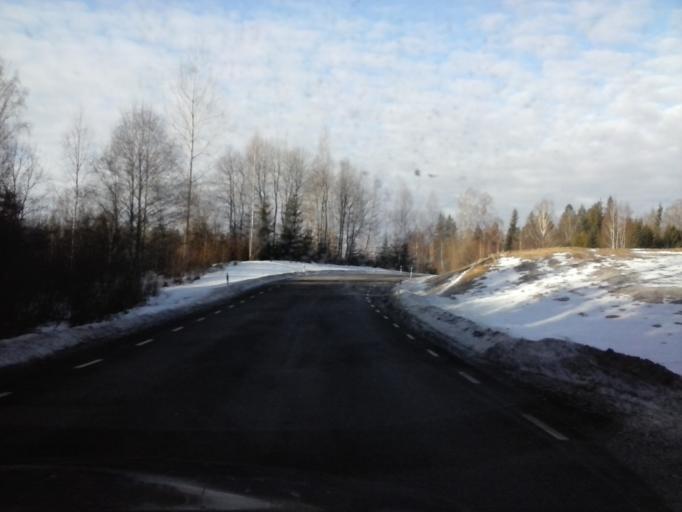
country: EE
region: Tartu
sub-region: Elva linn
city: Elva
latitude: 58.0471
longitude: 26.4086
